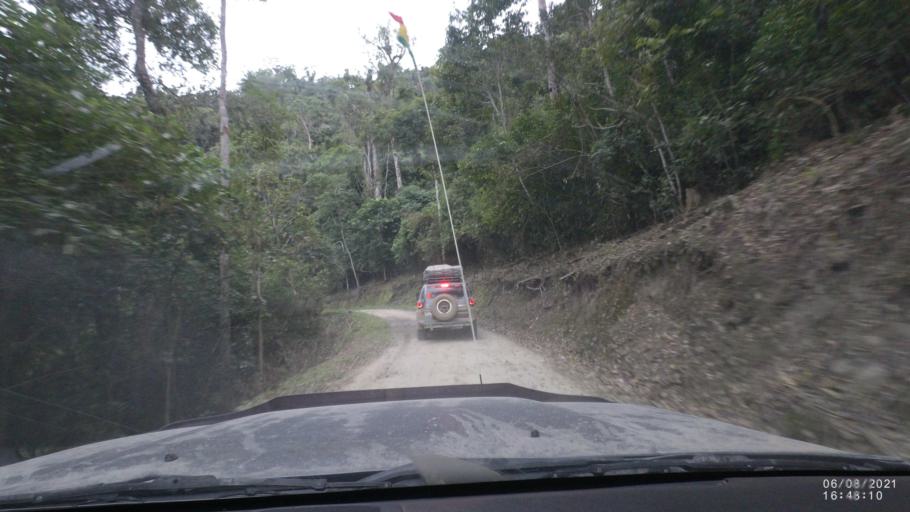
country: BO
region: La Paz
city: Quime
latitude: -16.5002
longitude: -66.7635
